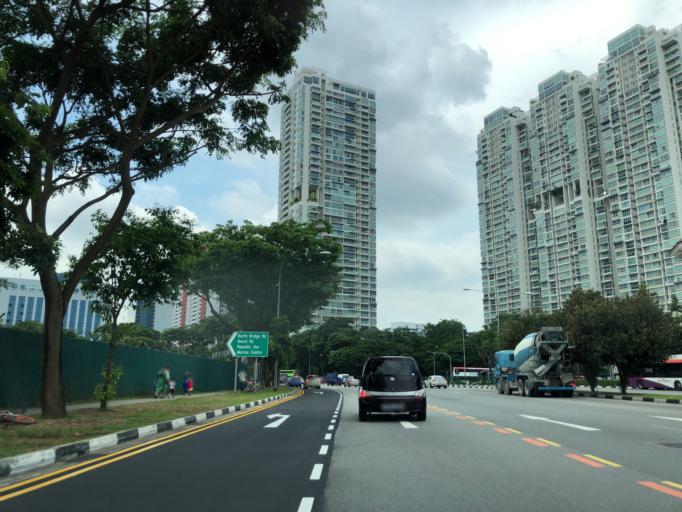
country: SG
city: Singapore
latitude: 1.3089
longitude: 103.8651
